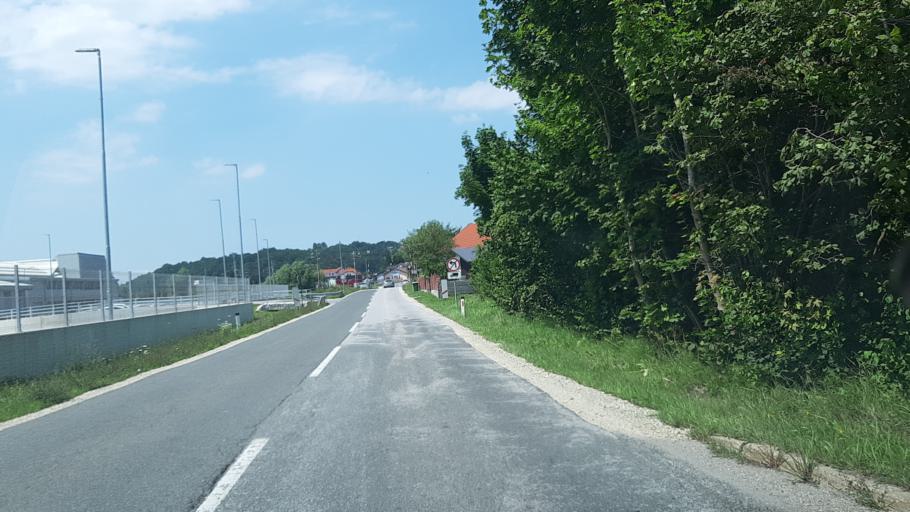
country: SI
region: Sentjur pri Celju
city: Sentjur
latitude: 46.2117
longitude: 15.4062
